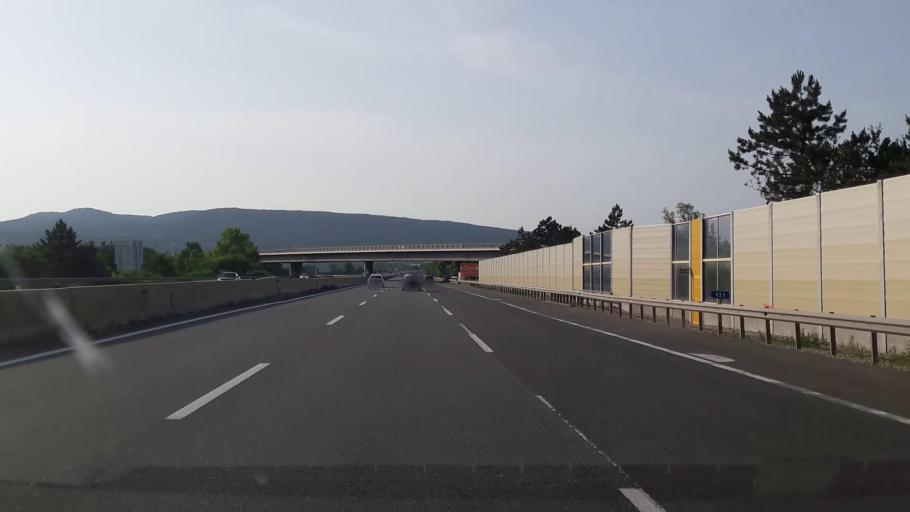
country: AT
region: Lower Austria
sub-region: Politischer Bezirk Wiener Neustadt
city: Weikersdorf am Steinfelde
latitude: 47.8170
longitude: 16.1920
